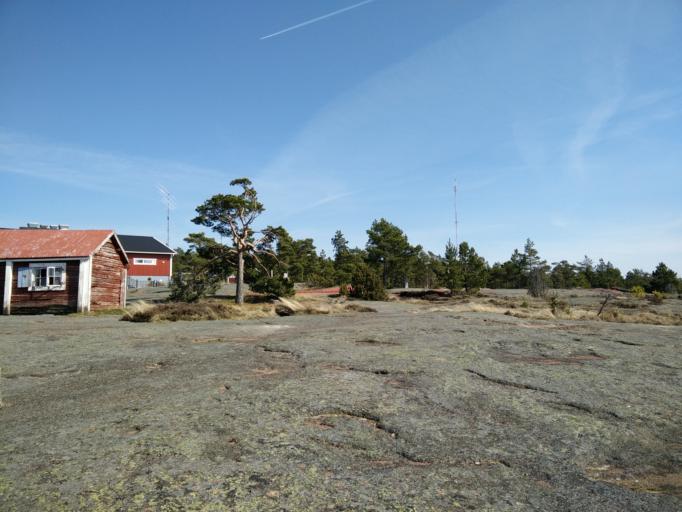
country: AX
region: Alands landsbygd
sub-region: Geta
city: Geta
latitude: 60.3860
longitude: 19.8427
